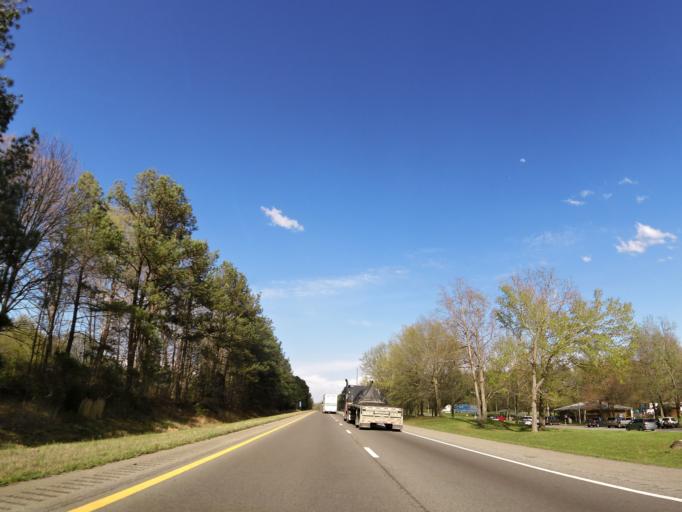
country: US
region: Tennessee
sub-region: Dickson County
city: Dickson
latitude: 36.0111
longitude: -87.3804
